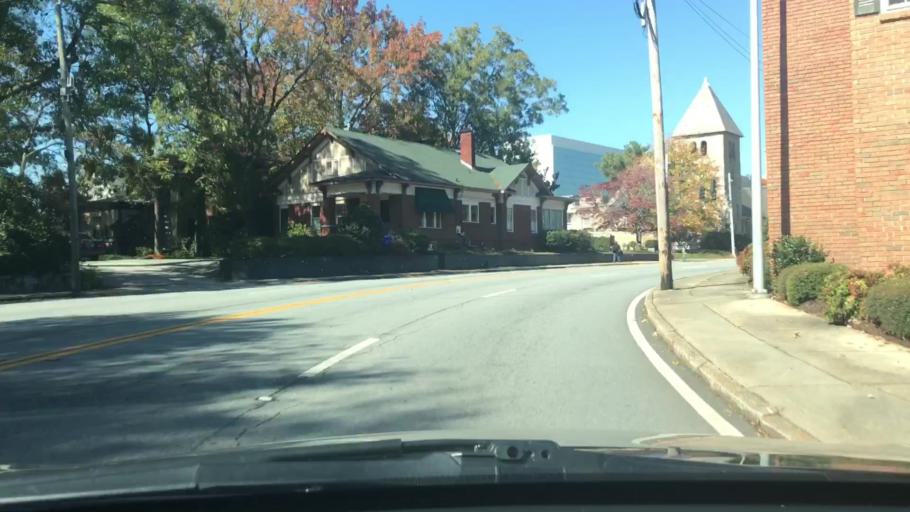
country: US
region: Georgia
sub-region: DeKalb County
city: Decatur
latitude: 33.7739
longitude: -84.2916
